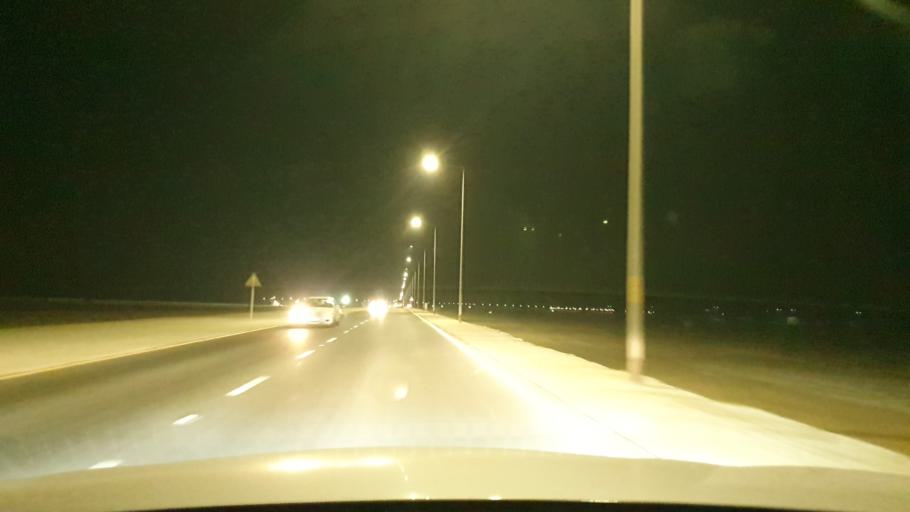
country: BH
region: Muharraq
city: Al Muharraq
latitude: 26.2792
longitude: 50.5932
